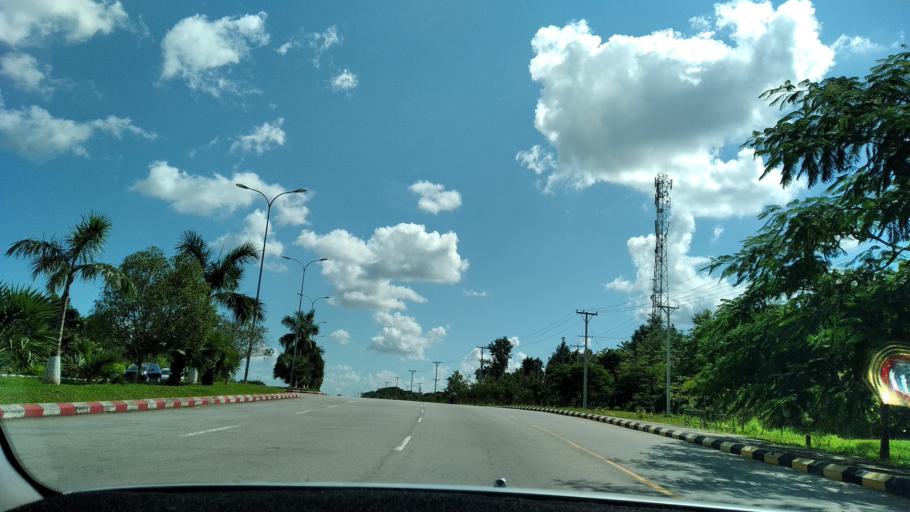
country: MM
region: Mandalay
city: Nay Pyi Taw
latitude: 19.7894
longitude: 96.1449
